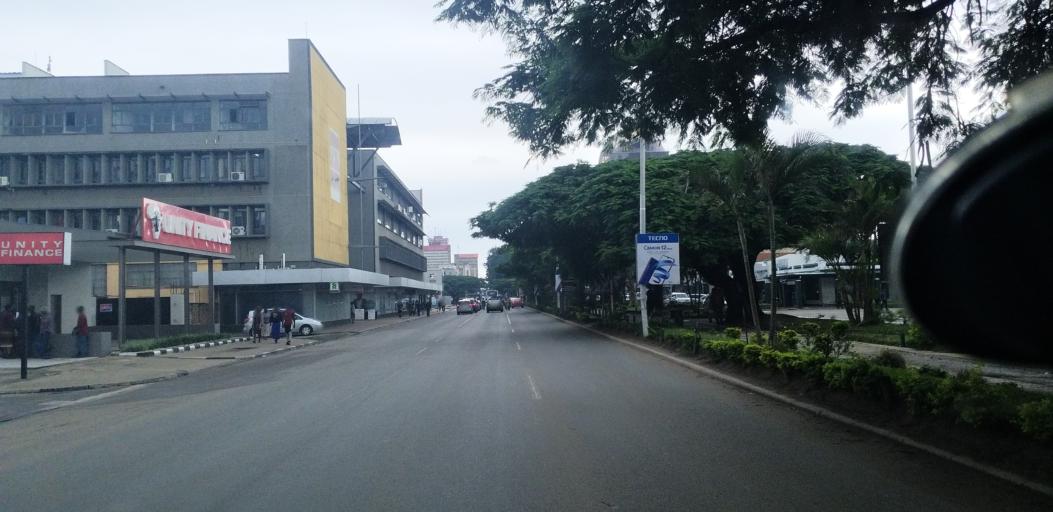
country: ZM
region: Lusaka
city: Lusaka
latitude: -15.4143
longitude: 28.2814
